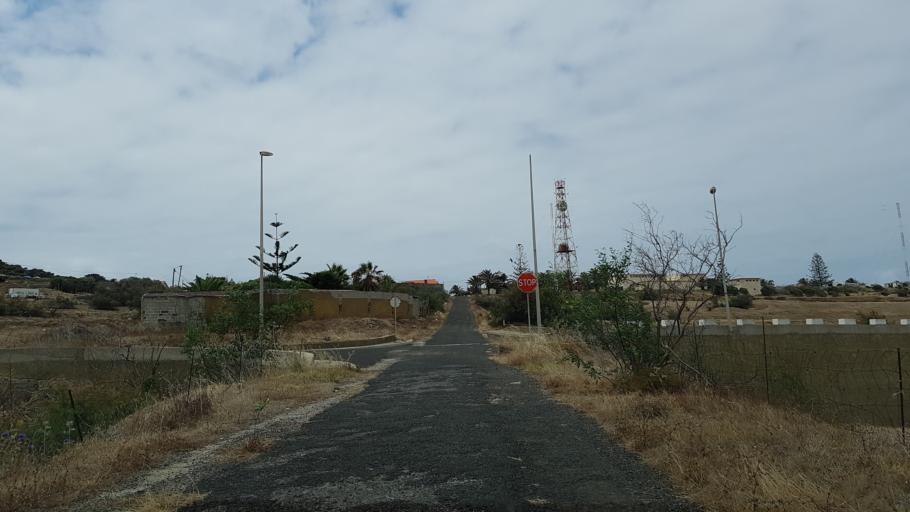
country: PT
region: Madeira
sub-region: Porto Santo
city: Camacha
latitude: 33.0891
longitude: -16.3368
